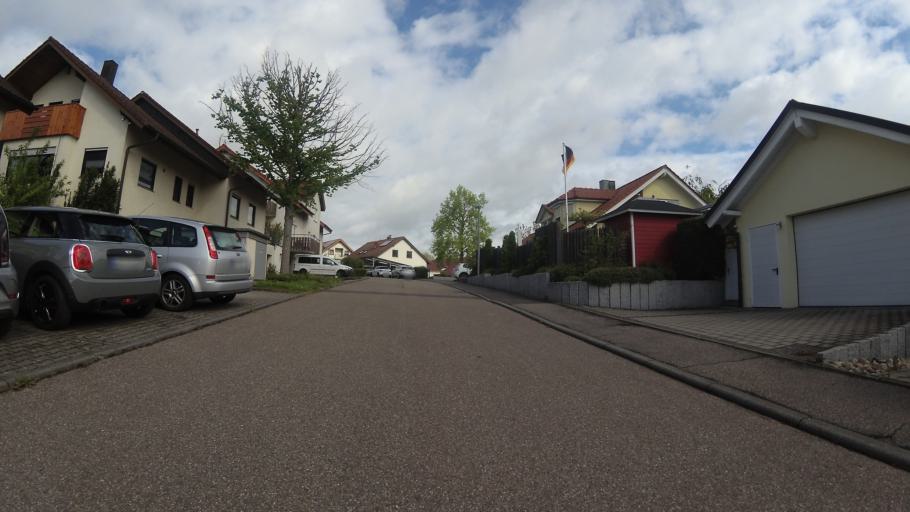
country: DE
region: Baden-Wuerttemberg
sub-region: Regierungsbezirk Stuttgart
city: Erlenbach
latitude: 49.1771
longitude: 9.2662
